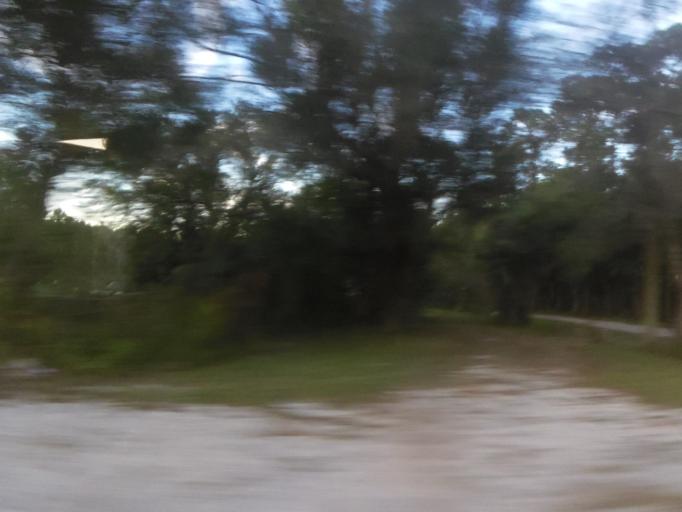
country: US
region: Florida
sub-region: Saint Johns County
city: Fruit Cove
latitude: 30.1045
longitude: -81.5138
